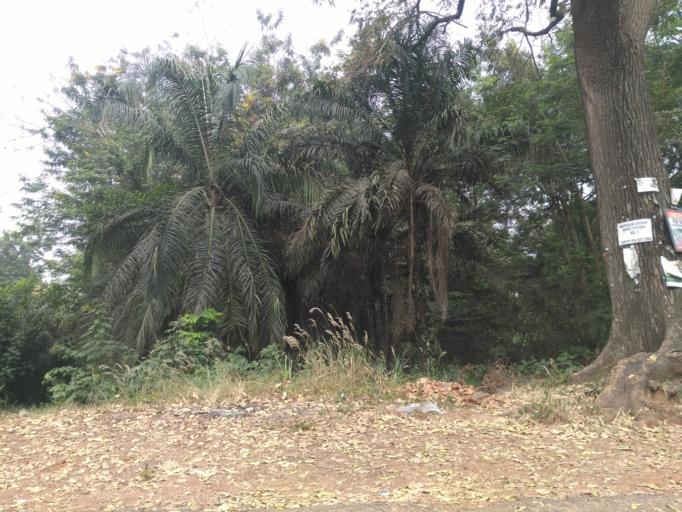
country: GH
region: Ashanti
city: Kumasi
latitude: 6.6866
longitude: -1.6296
